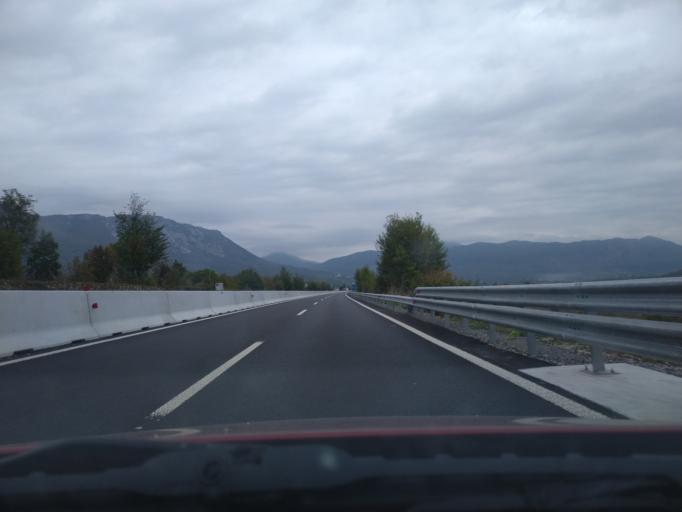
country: SI
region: Ajdovscina
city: Lokavec
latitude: 45.8840
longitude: 13.8831
